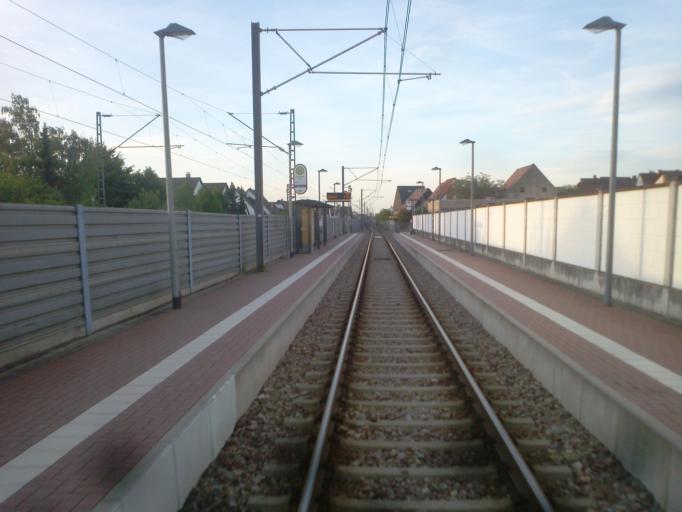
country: DE
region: Baden-Wuerttemberg
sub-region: Karlsruhe Region
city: Karlsdorf-Neuthard
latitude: 49.1039
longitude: 8.4750
